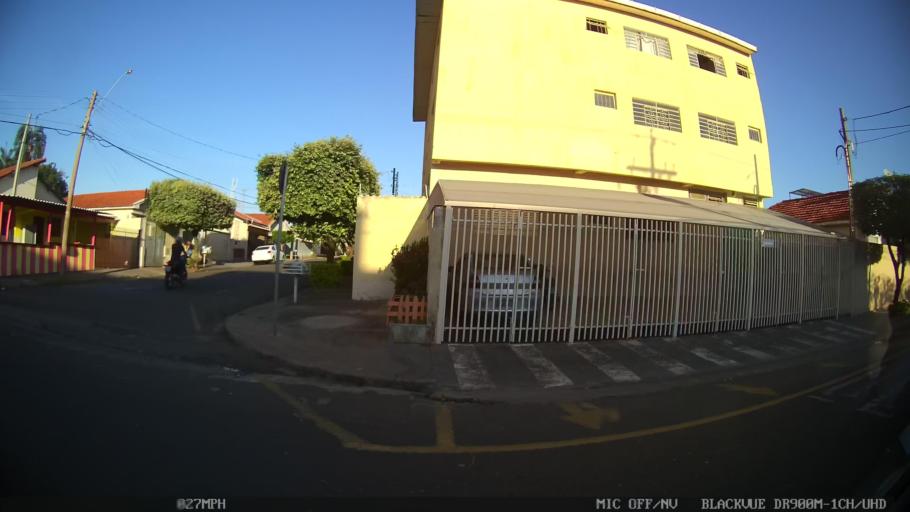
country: BR
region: Sao Paulo
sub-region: Sao Jose Do Rio Preto
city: Sao Jose do Rio Preto
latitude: -20.7937
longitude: -49.3657
